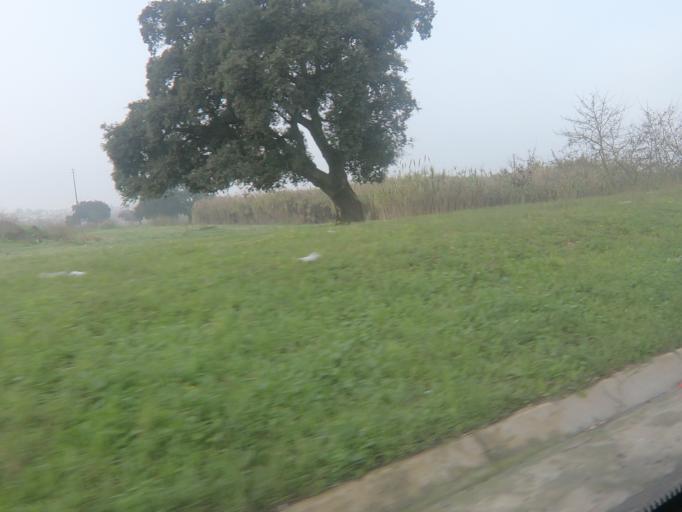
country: PT
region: Setubal
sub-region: Montijo
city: Montijo
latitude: 38.6884
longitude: -8.9460
